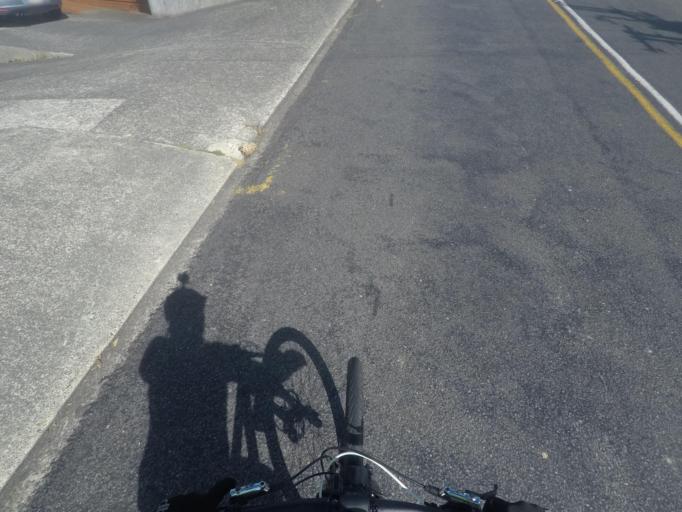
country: NZ
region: Auckland
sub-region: Auckland
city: Auckland
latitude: -36.9234
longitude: 174.7629
